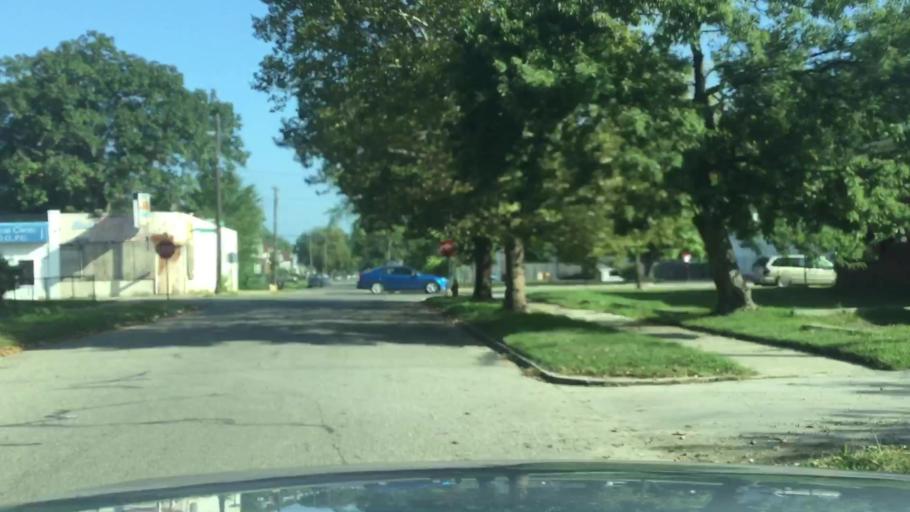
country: US
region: Michigan
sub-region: Oakland County
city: Hazel Park
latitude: 42.4395
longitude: -83.0879
